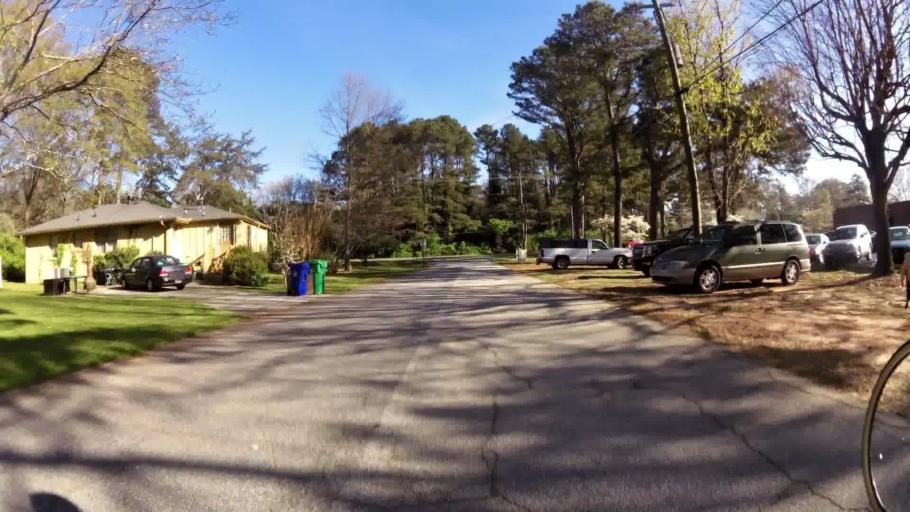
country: US
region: Georgia
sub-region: DeKalb County
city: Clarkston
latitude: 33.8400
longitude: -84.2654
